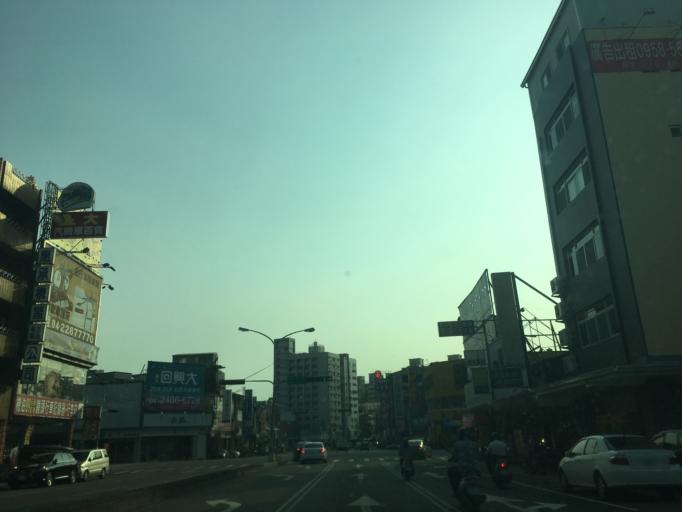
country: TW
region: Taiwan
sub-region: Taichung City
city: Taichung
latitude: 24.1274
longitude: 120.6798
